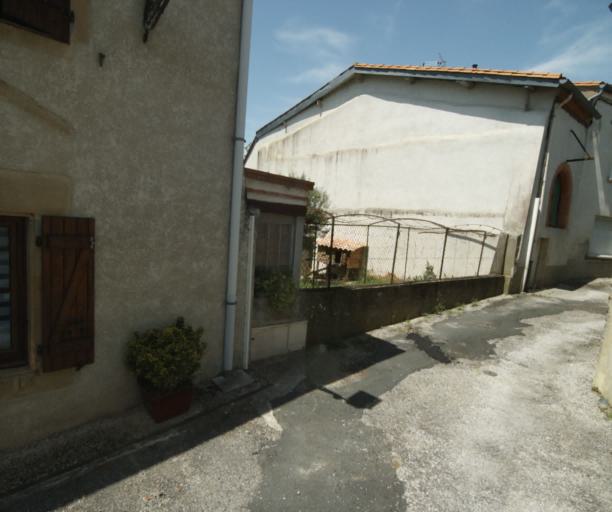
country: FR
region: Midi-Pyrenees
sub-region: Departement de la Haute-Garonne
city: Saint-Felix-Lauragais
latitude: 43.4566
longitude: 1.8360
